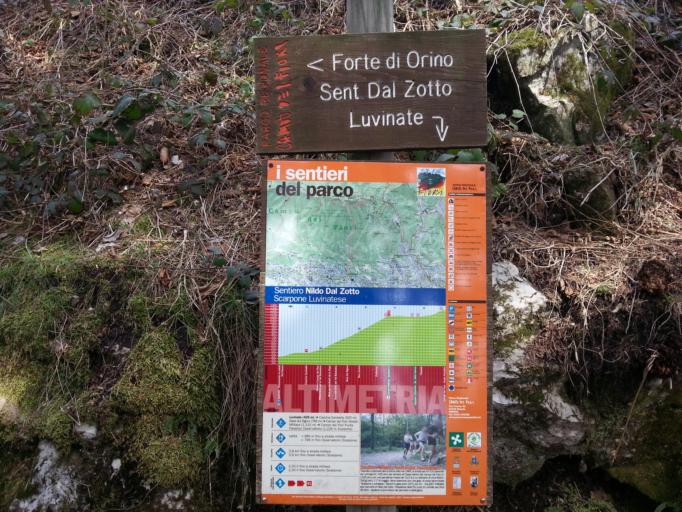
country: IT
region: Lombardy
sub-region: Provincia di Varese
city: Castello Cabiaglio
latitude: 45.8675
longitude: 8.7661
